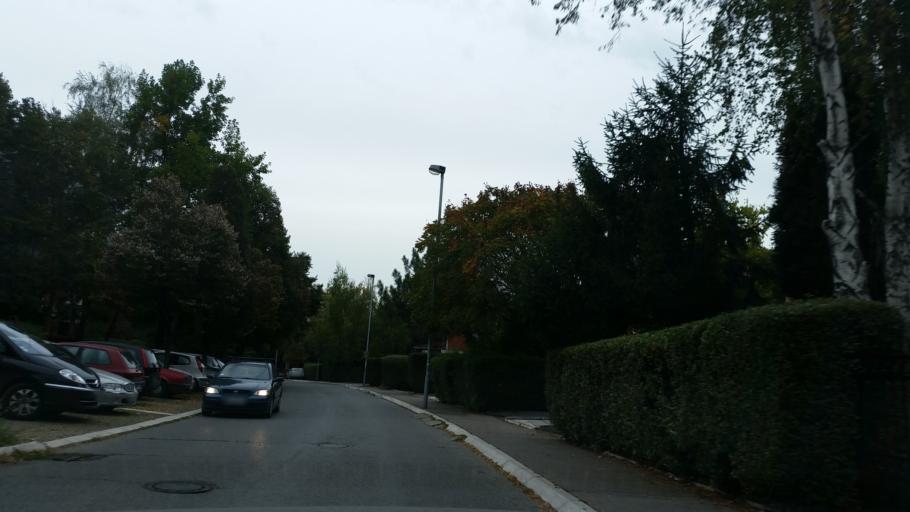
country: RS
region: Central Serbia
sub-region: Belgrade
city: Zemun
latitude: 44.8207
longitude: 20.3910
